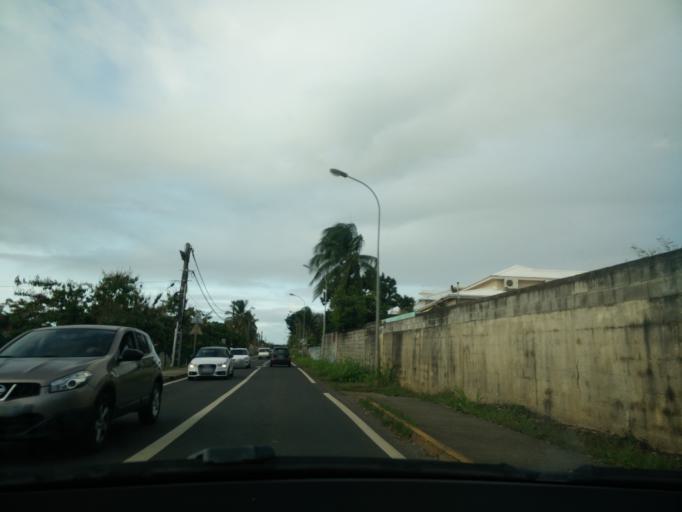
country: GP
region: Guadeloupe
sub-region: Guadeloupe
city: Baie-Mahault
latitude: 16.2381
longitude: -61.6024
